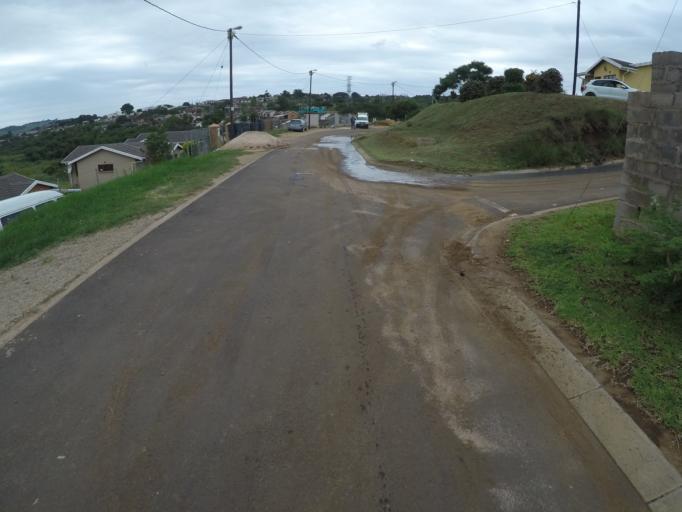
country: ZA
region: KwaZulu-Natal
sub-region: uThungulu District Municipality
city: Empangeni
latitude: -28.7709
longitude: 31.8732
